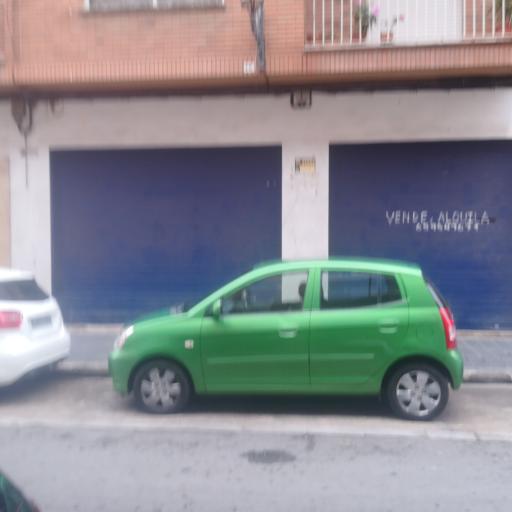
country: ES
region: Valencia
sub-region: Provincia de Valencia
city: Valencia
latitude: 39.4558
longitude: -0.3893
